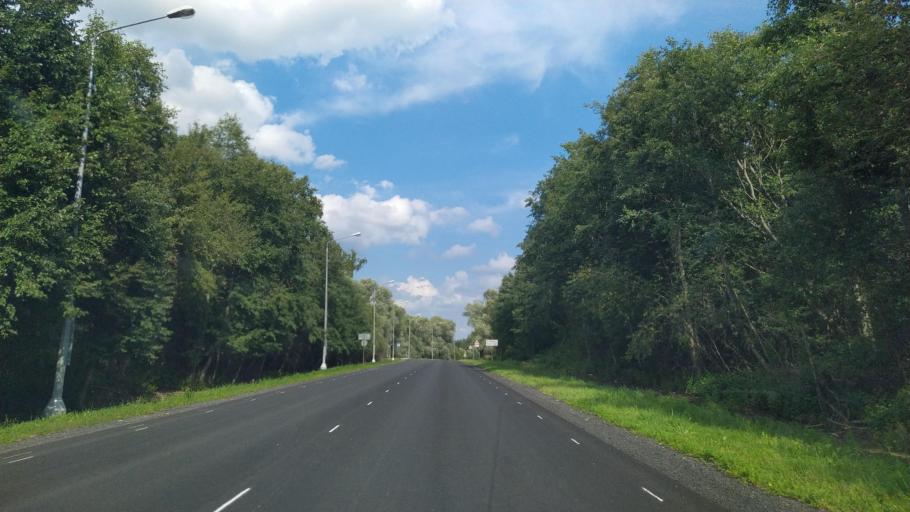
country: RU
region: Pskov
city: Porkhov
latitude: 57.7301
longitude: 29.3805
